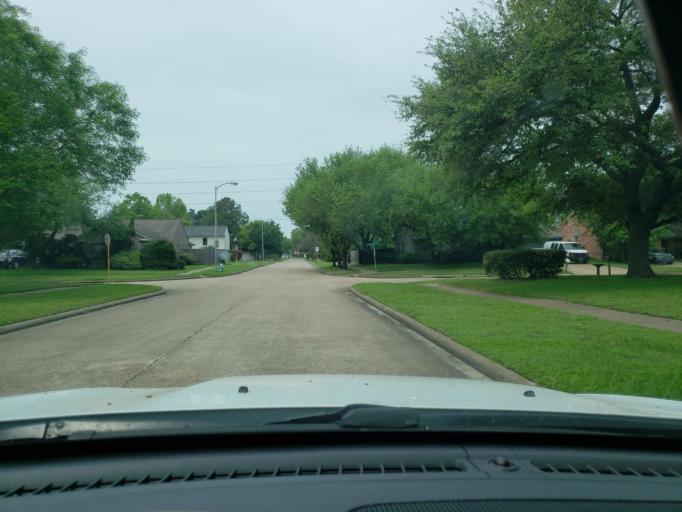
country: US
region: Texas
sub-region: Harris County
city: Jersey Village
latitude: 29.9173
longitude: -95.5743
